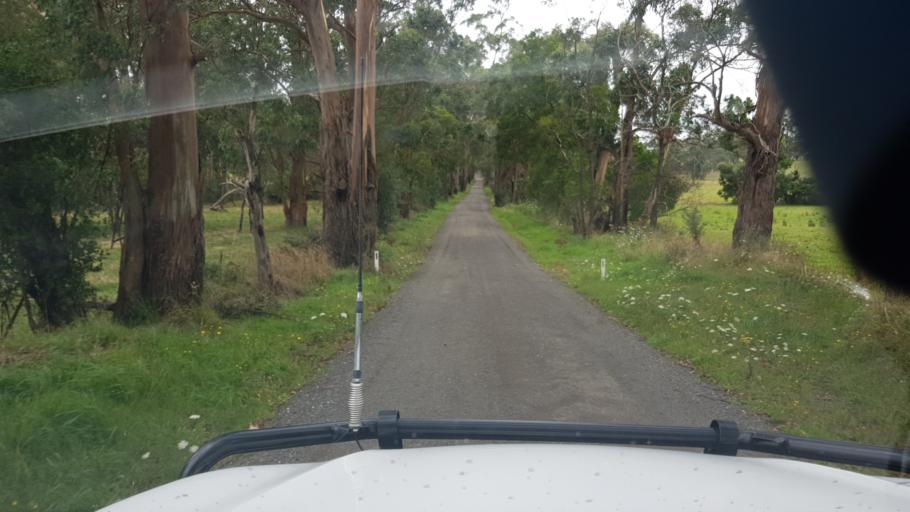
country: AU
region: Victoria
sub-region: Baw Baw
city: Warragul
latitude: -38.1847
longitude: 145.8743
